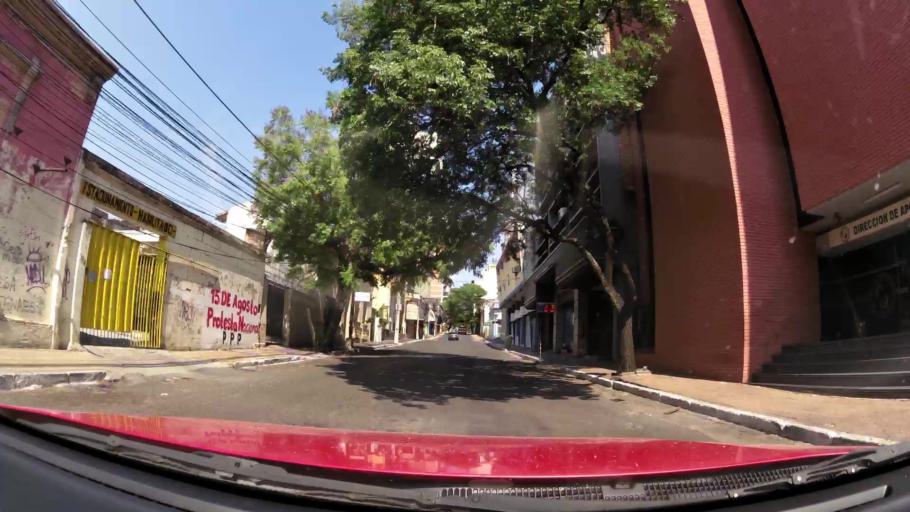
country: PY
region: Asuncion
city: Asuncion
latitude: -25.2850
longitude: -57.6362
